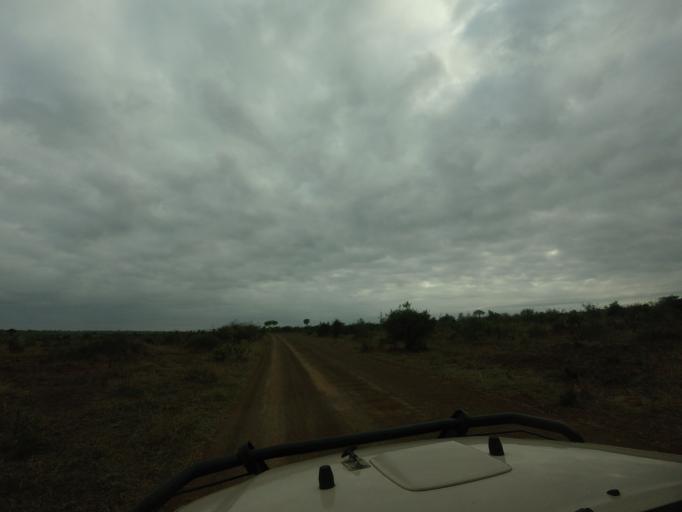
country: ZA
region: Mpumalanga
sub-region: Ehlanzeni District
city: Komatipoort
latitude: -25.3185
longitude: 31.9087
